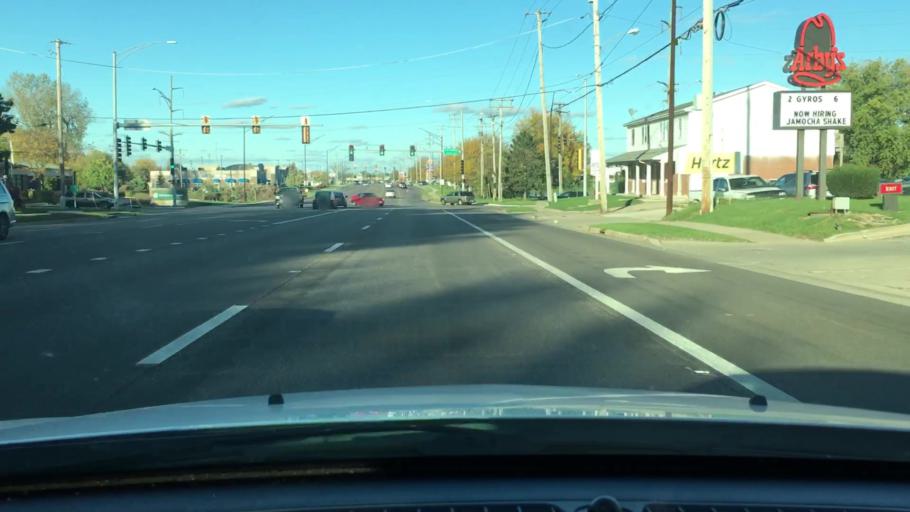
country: US
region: Illinois
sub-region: DeKalb County
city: DeKalb
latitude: 41.9487
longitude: -88.7298
